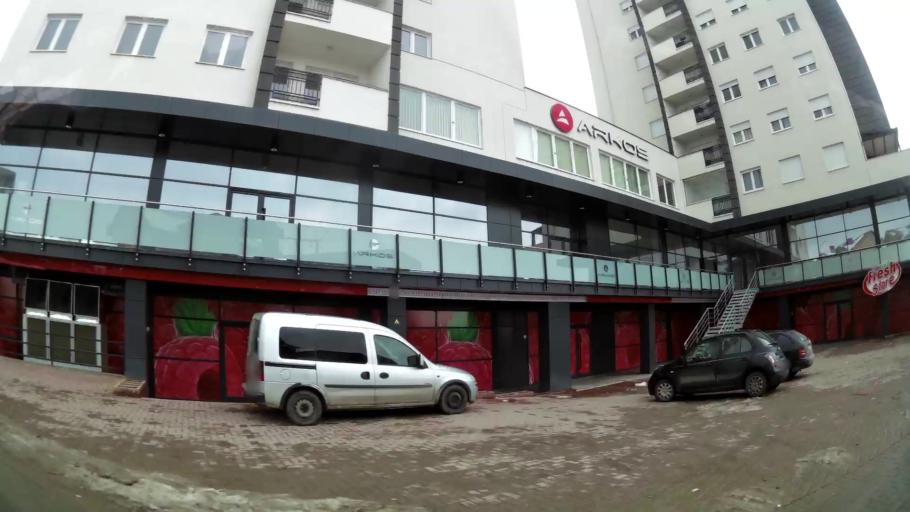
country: XK
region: Pristina
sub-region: Komuna e Prishtines
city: Pristina
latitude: 42.6547
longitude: 21.1900
